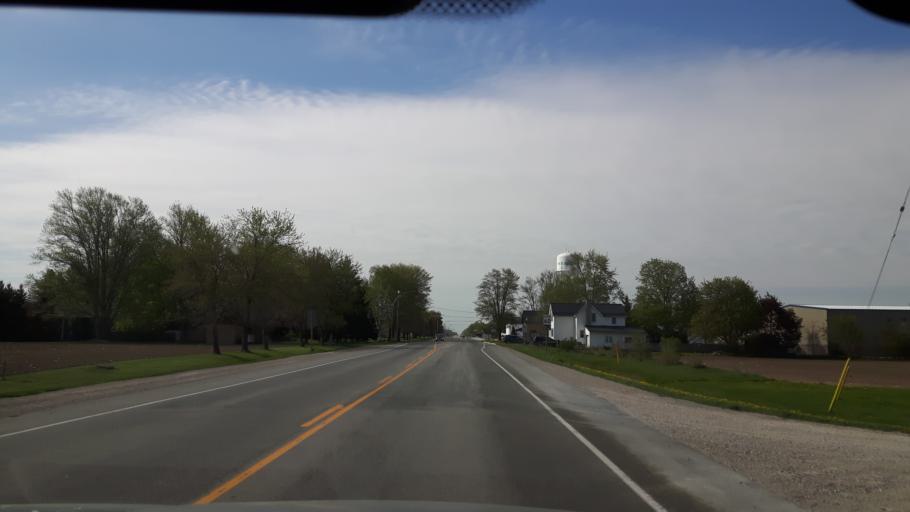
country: CA
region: Ontario
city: Bluewater
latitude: 43.4393
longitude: -81.4996
